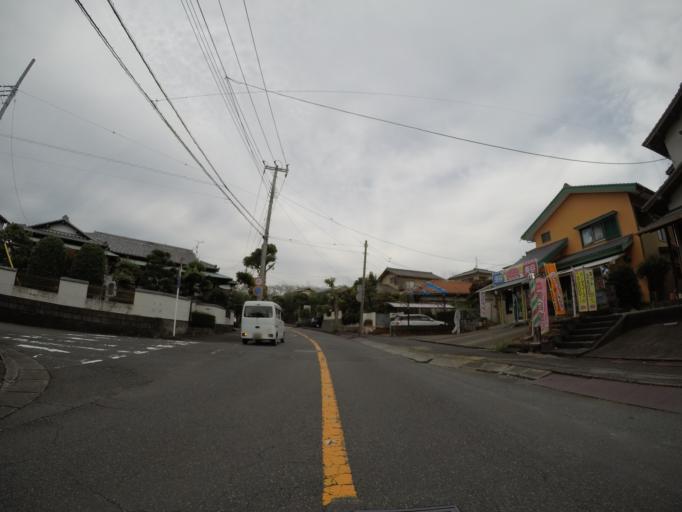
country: JP
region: Shizuoka
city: Fuji
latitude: 35.1818
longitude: 138.7096
